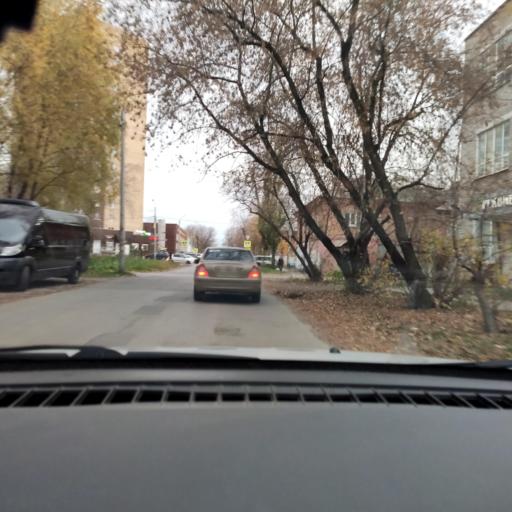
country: RU
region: Perm
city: Perm
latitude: 58.1086
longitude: 56.3803
